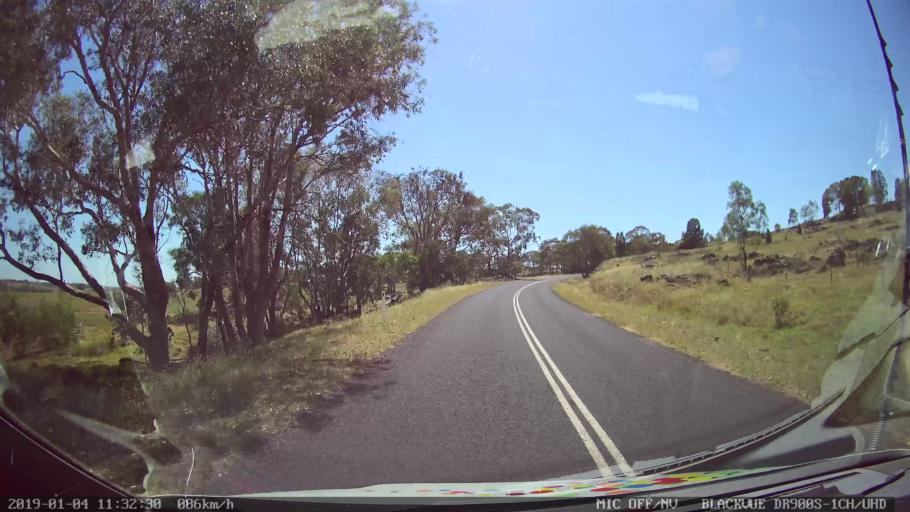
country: AU
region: New South Wales
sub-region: Cabonne
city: Molong
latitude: -33.0629
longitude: 148.8037
